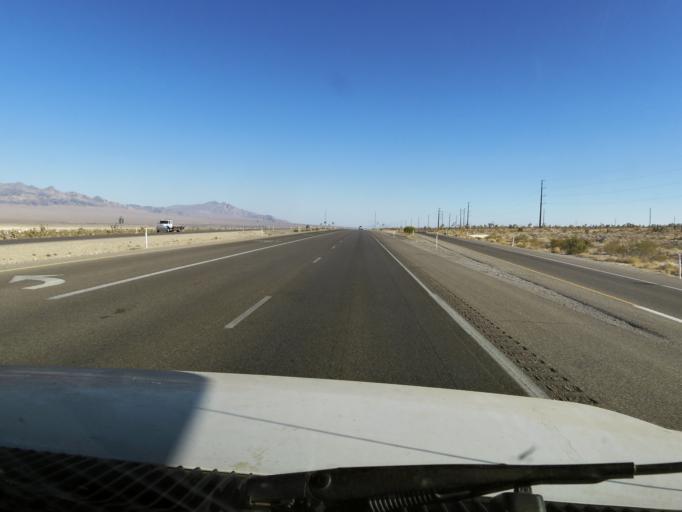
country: US
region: Nevada
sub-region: Clark County
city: Summerlin South
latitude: 36.4787
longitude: -115.4708
